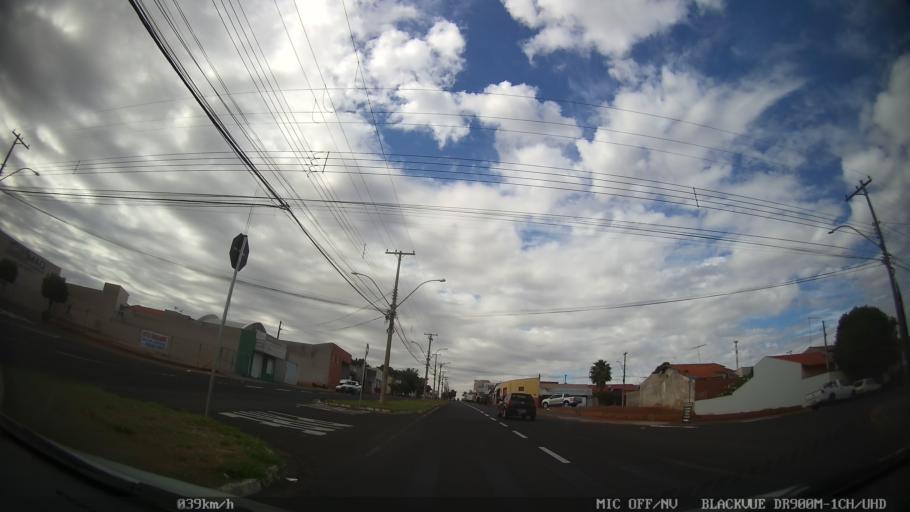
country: BR
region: Sao Paulo
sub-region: Sao Jose Do Rio Preto
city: Sao Jose do Rio Preto
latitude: -20.8036
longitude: -49.5005
